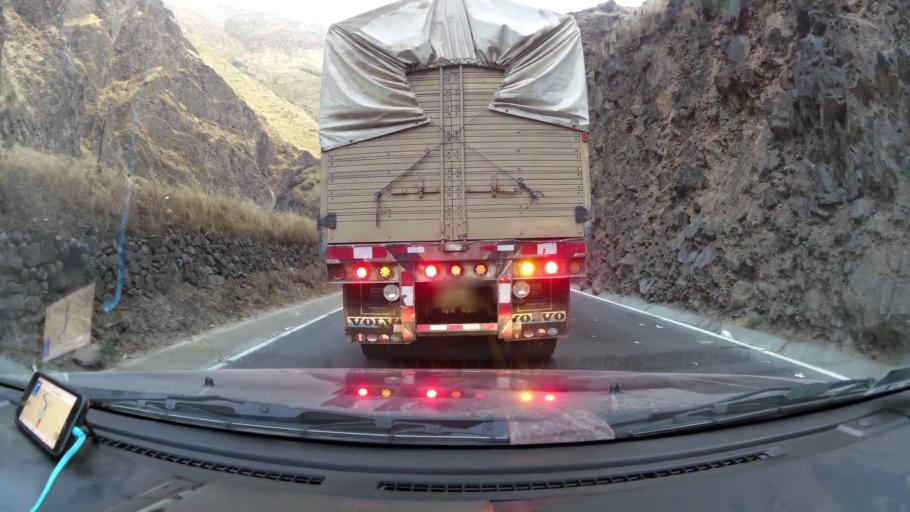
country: PE
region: Lima
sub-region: Provincia de Huarochiri
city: San Mateo
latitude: -11.8071
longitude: -76.3423
